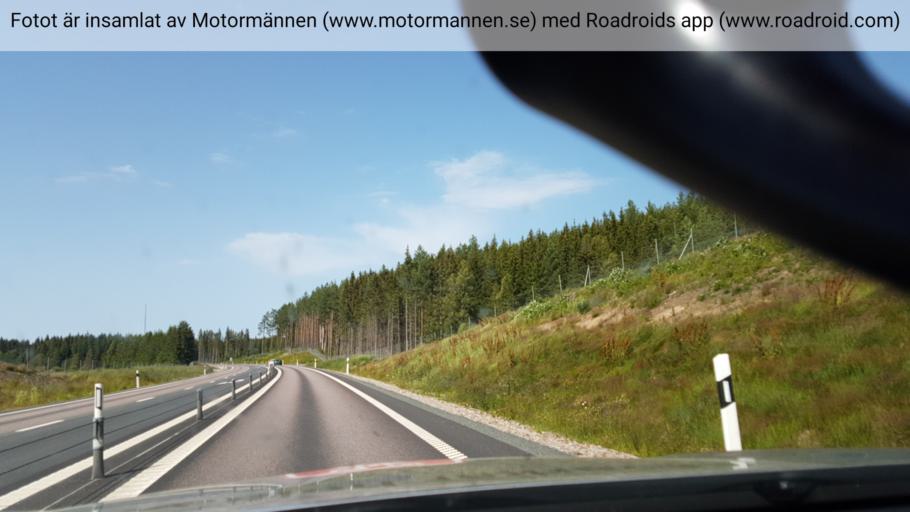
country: SE
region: Joenkoeping
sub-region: Aneby Kommun
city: Aneby
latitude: 57.8337
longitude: 14.8745
